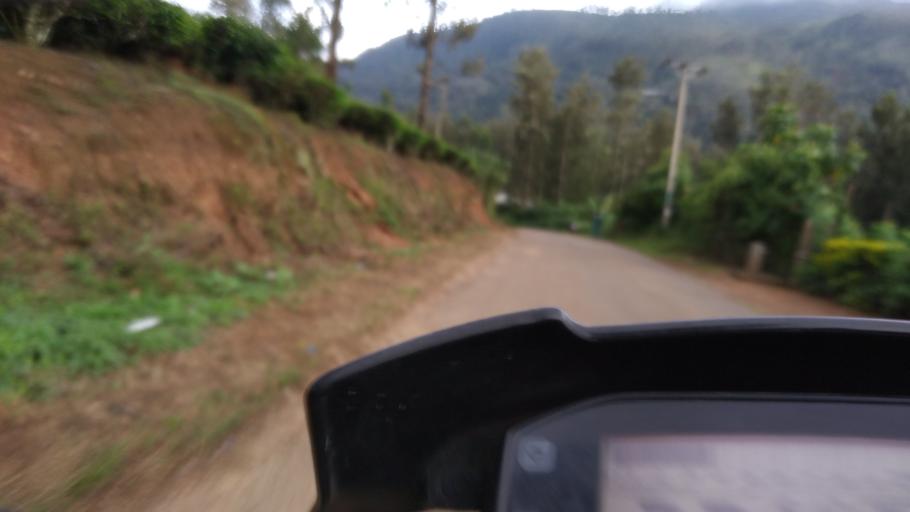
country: IN
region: Tamil Nadu
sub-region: Theni
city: Bodinayakkanur
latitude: 10.0237
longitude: 77.2405
